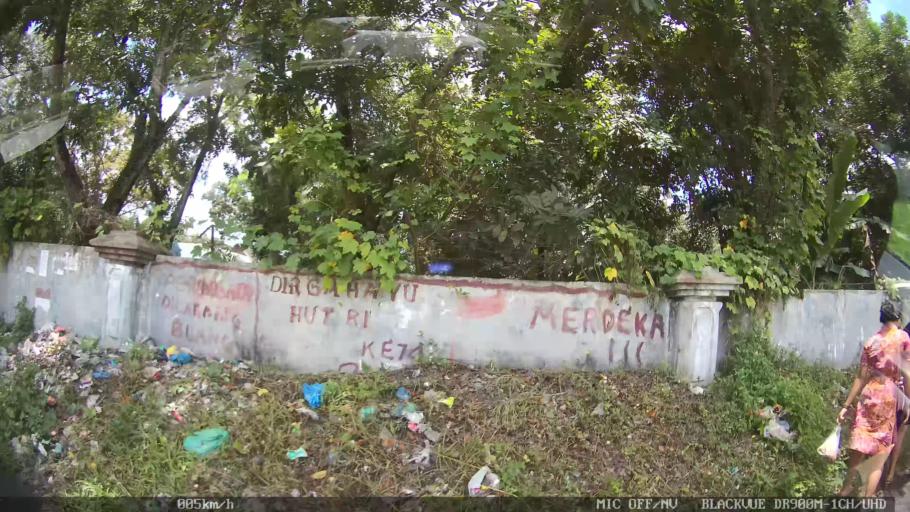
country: ID
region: North Sumatra
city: Medan
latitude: 3.6062
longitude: 98.7205
